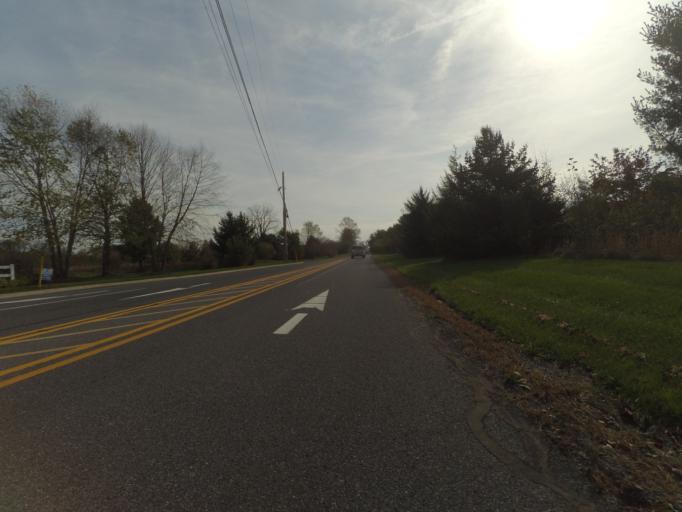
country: US
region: Pennsylvania
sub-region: Centre County
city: Houserville
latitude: 40.8537
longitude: -77.8695
